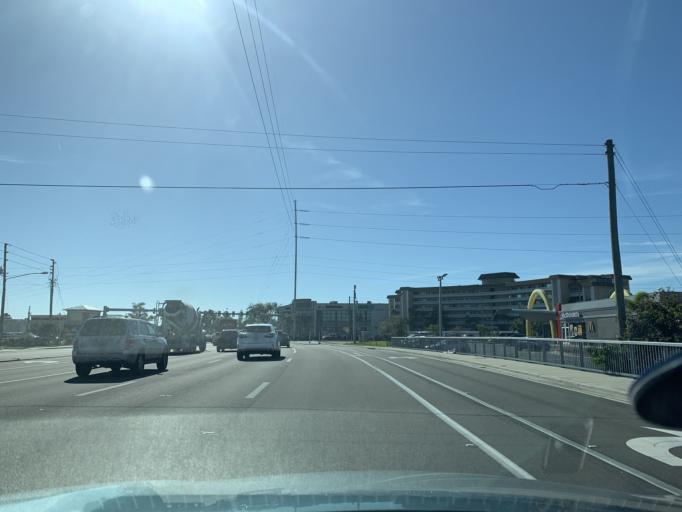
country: US
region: Florida
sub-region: Pinellas County
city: Seminole
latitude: 27.8405
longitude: -82.7626
